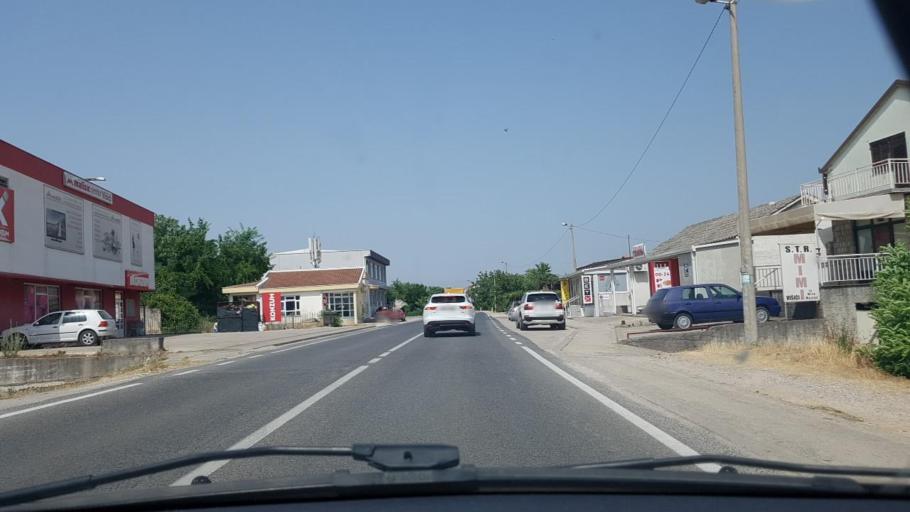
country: BA
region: Federation of Bosnia and Herzegovina
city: Tasovcici
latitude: 43.0669
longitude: 17.7114
